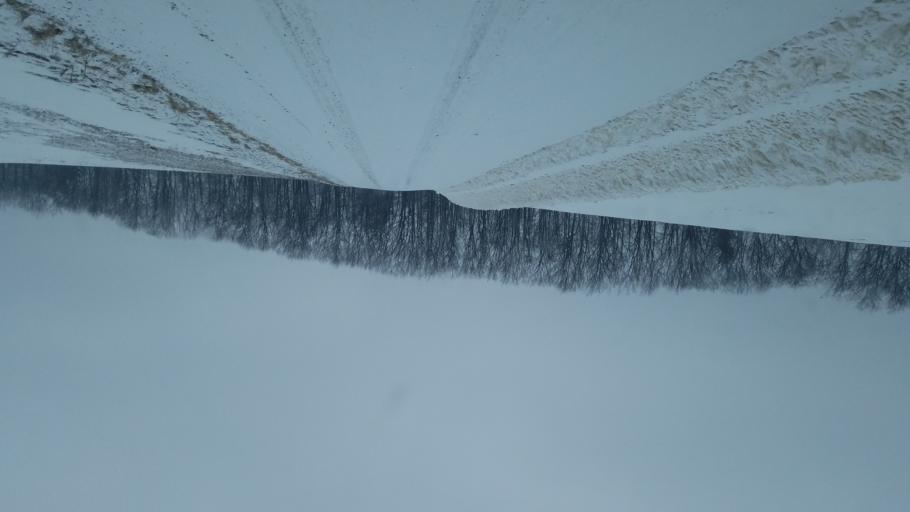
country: US
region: New York
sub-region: Steuben County
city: Canisteo
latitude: 42.1153
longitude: -77.5110
